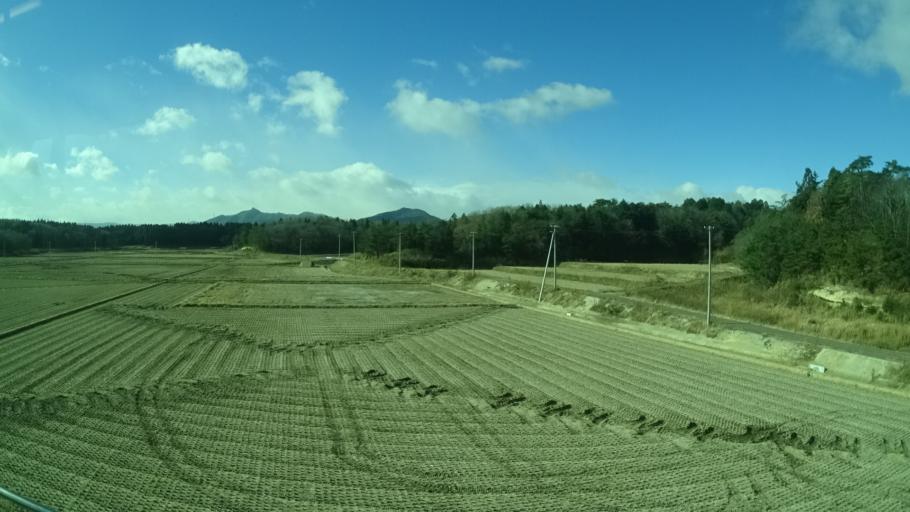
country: JP
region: Miyagi
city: Watari
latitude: 37.9018
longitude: 140.9163
